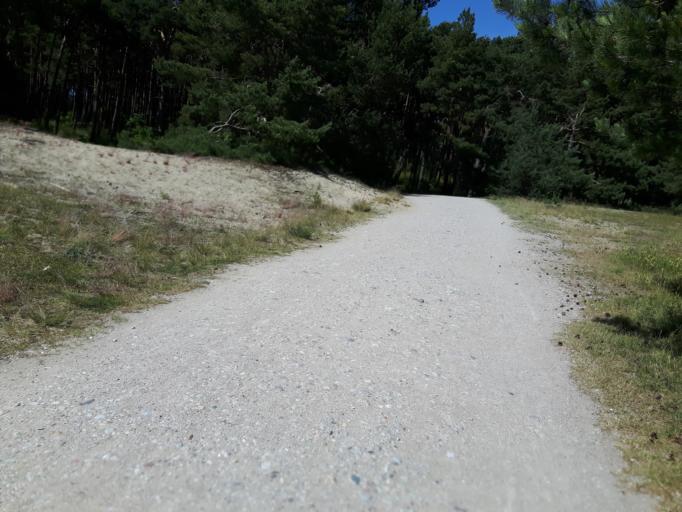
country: LT
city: Nida
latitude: 55.2978
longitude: 20.9974
